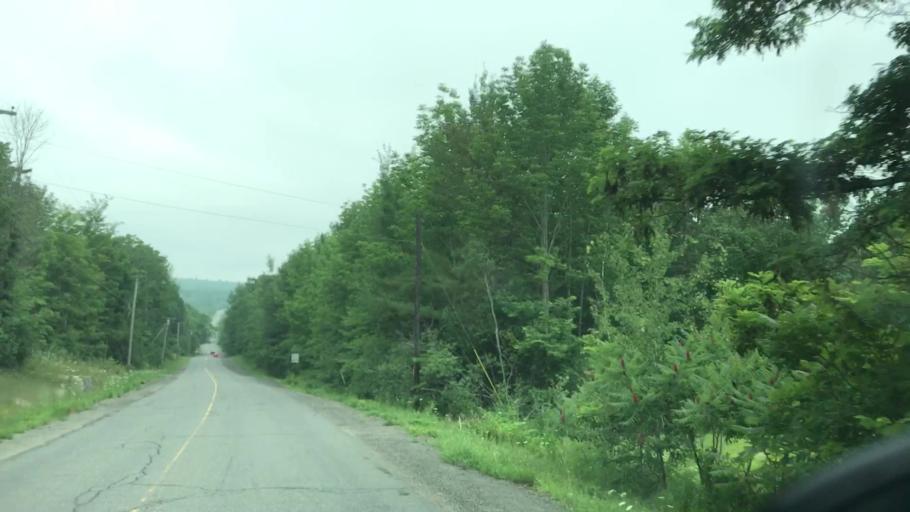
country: US
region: Maine
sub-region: Penobscot County
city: Veazie
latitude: 44.8783
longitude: -68.7124
